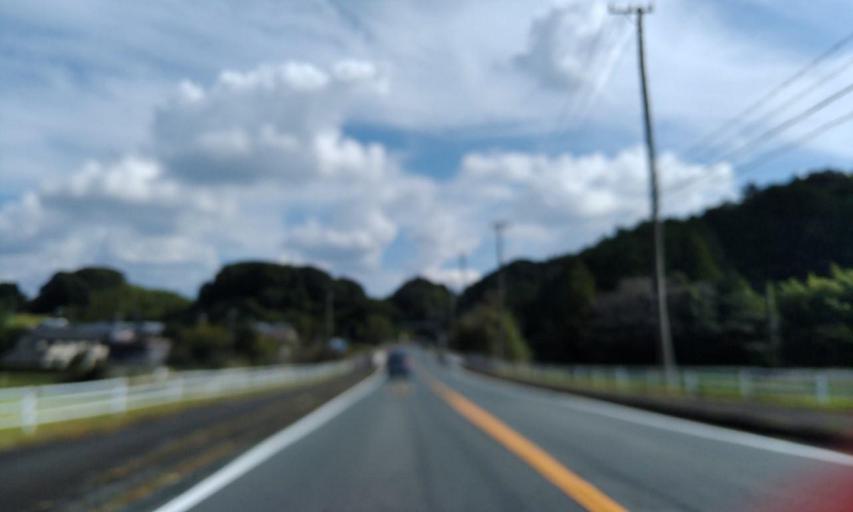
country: JP
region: Shizuoka
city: Mori
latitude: 34.8246
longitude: 137.8987
